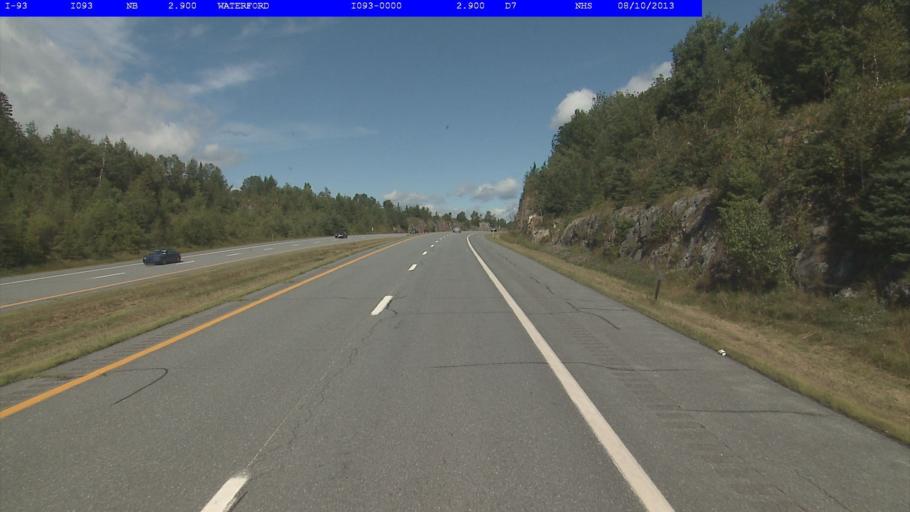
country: US
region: Vermont
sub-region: Caledonia County
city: Saint Johnsbury
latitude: 44.3790
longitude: -71.9177
